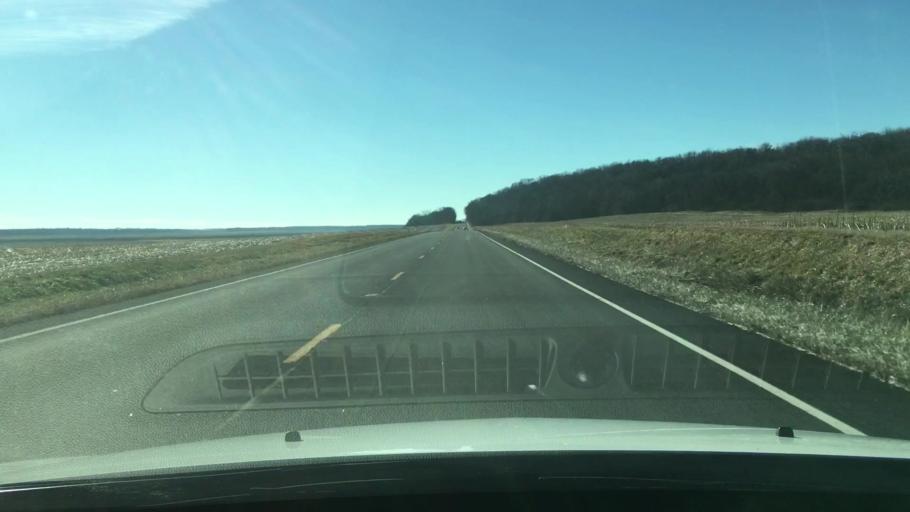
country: US
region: Illinois
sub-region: Fulton County
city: Canton
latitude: 40.4402
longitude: -89.9673
